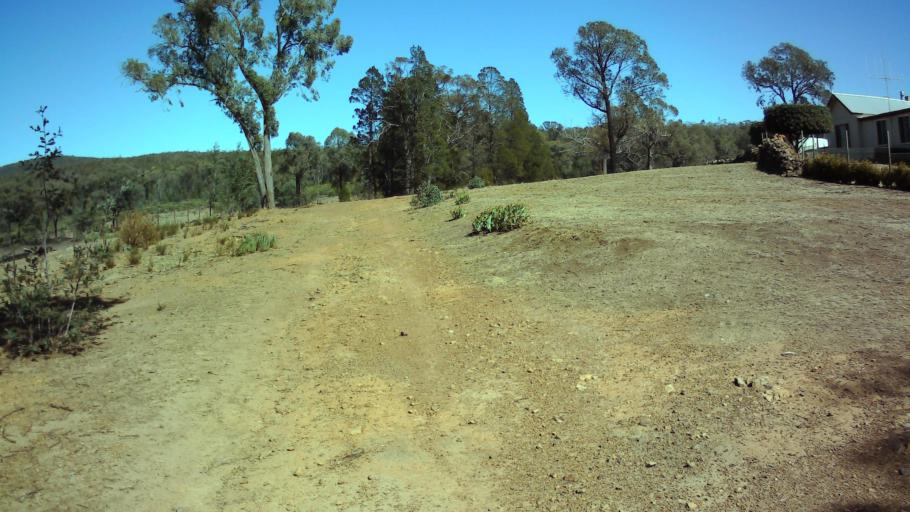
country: AU
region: New South Wales
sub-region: Weddin
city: Grenfell
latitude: -33.7409
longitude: 148.3678
